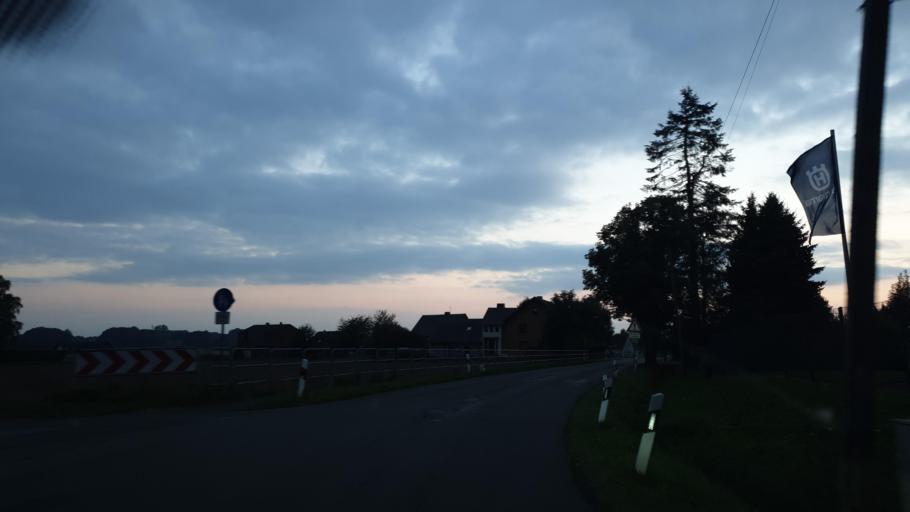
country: DE
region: North Rhine-Westphalia
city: Loehne
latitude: 52.2485
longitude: 8.7335
